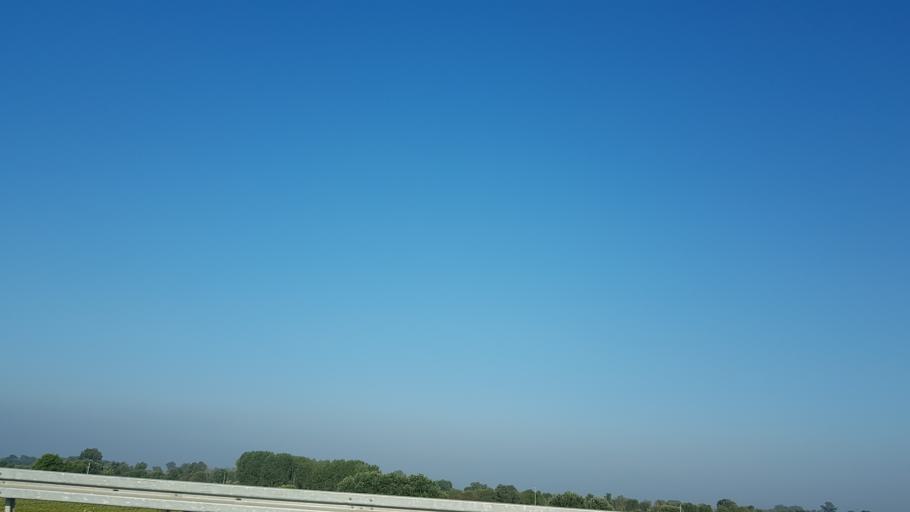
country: TR
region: Bursa
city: Tatkavakli
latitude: 40.1114
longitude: 28.2771
